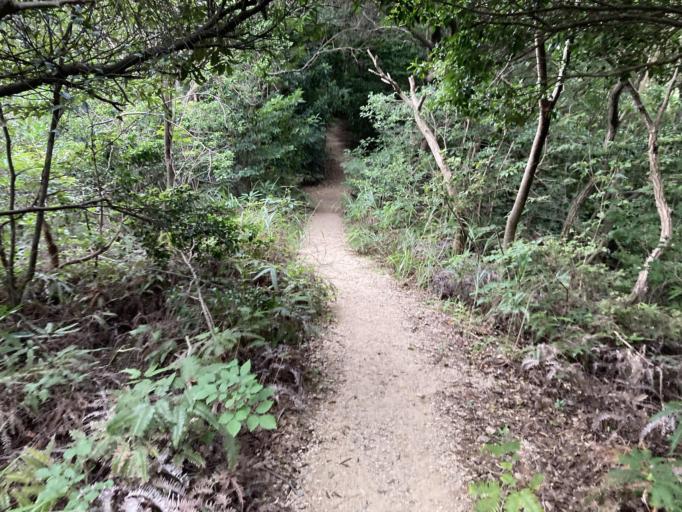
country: JP
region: Aichi
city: Nishio
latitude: 34.8483
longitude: 137.1198
